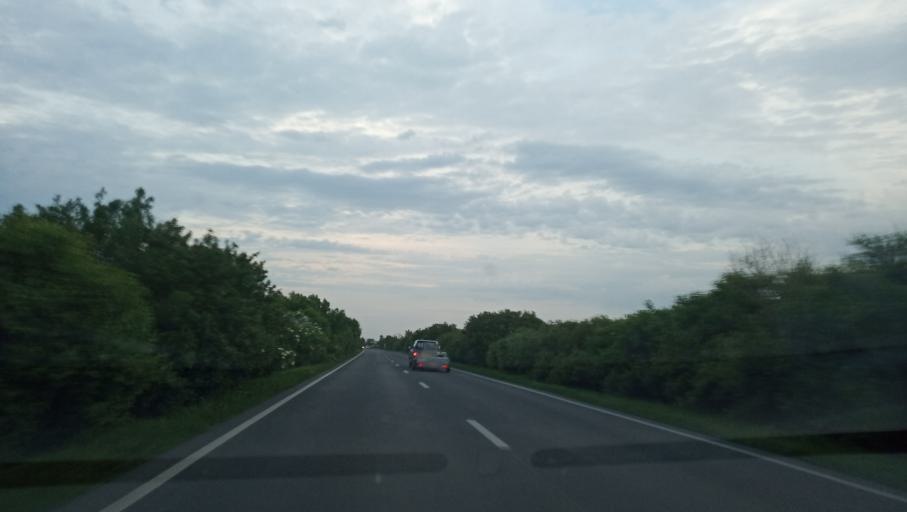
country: RO
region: Timis
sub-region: Comuna Voiteg
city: Voiteg
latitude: 45.5018
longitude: 21.2376
